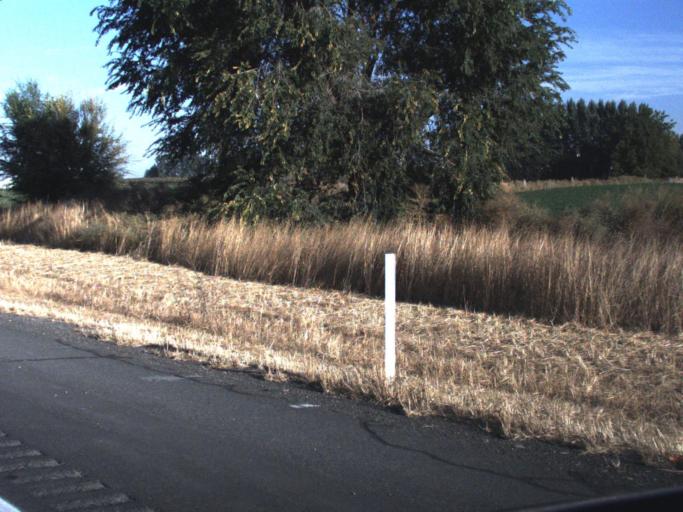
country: US
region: Washington
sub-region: Yakima County
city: Granger
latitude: 46.3539
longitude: -120.1934
